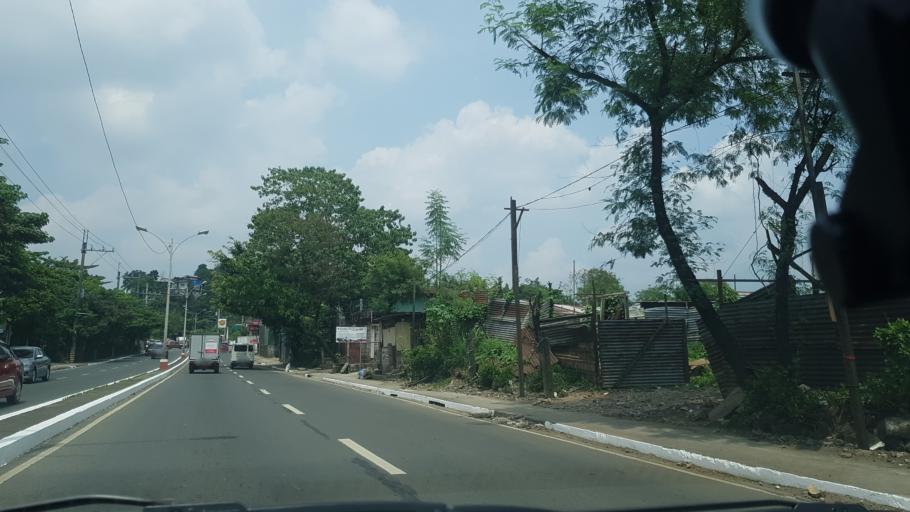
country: PH
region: Calabarzon
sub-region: Province of Rizal
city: San Mateo
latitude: 14.6830
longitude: 121.1061
